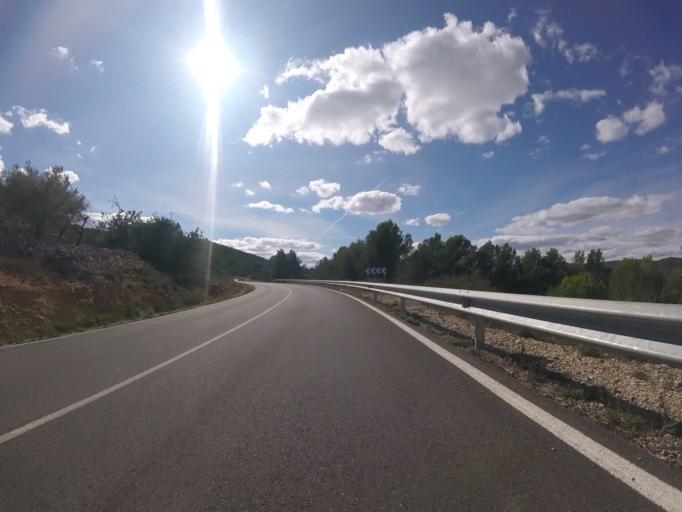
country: ES
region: Valencia
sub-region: Provincia de Castello
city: Cati
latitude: 40.4298
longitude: 0.0924
